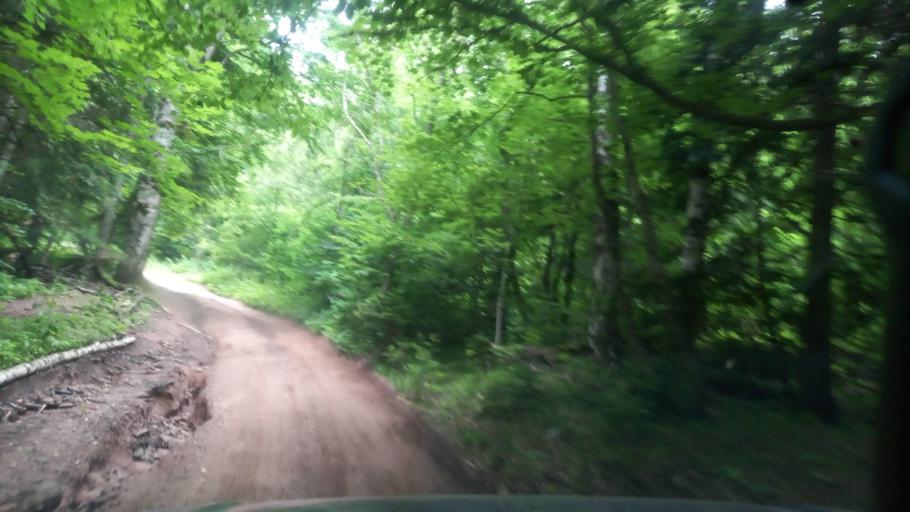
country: RU
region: Karachayevo-Cherkesiya
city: Kurdzhinovo
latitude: 43.8076
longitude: 40.8591
